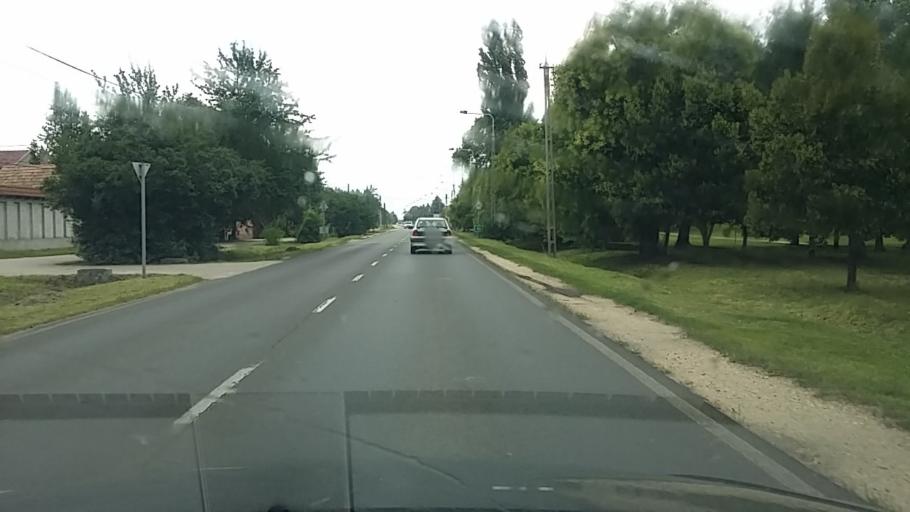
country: HU
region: Pest
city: Orkeny
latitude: 47.1293
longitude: 19.4240
